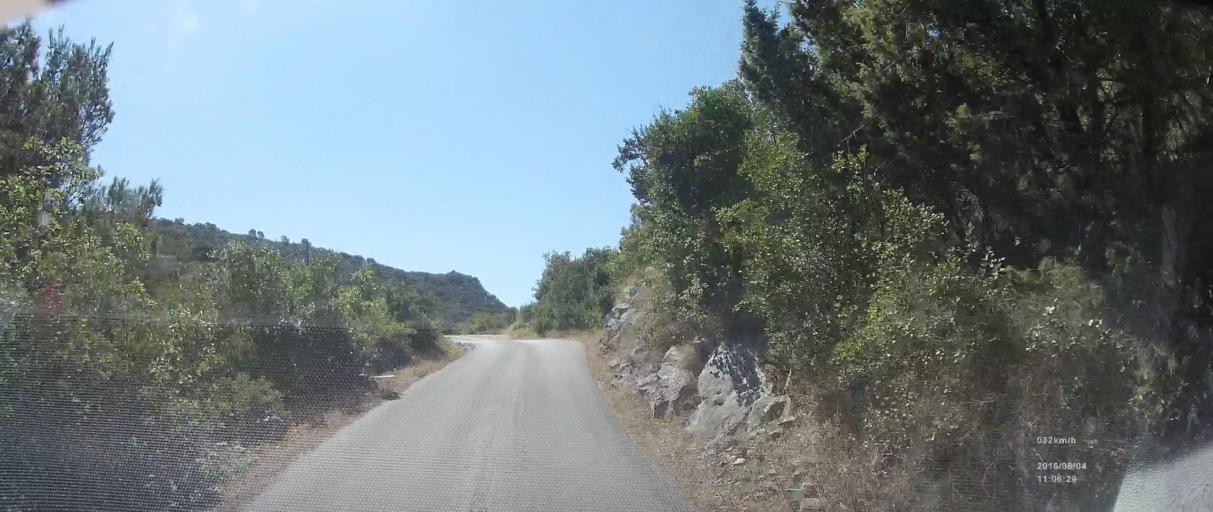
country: HR
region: Dubrovacko-Neretvanska
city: Blato
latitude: 42.7716
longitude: 17.4648
